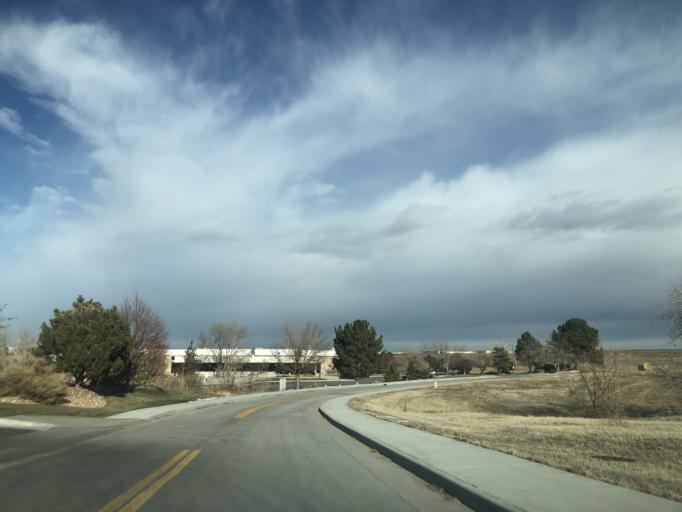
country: US
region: Colorado
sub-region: Douglas County
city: Meridian
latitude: 39.5488
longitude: -104.8616
